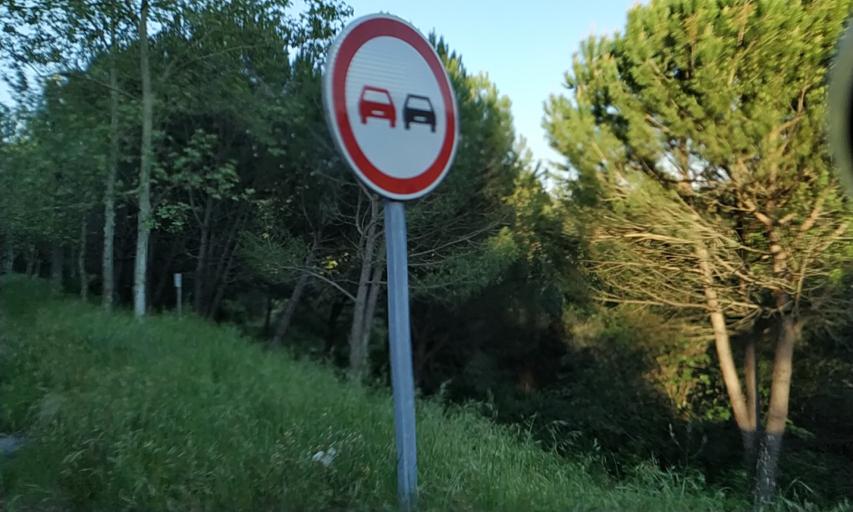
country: PT
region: Portalegre
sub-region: Marvao
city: Marvao
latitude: 39.3666
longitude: -7.3908
